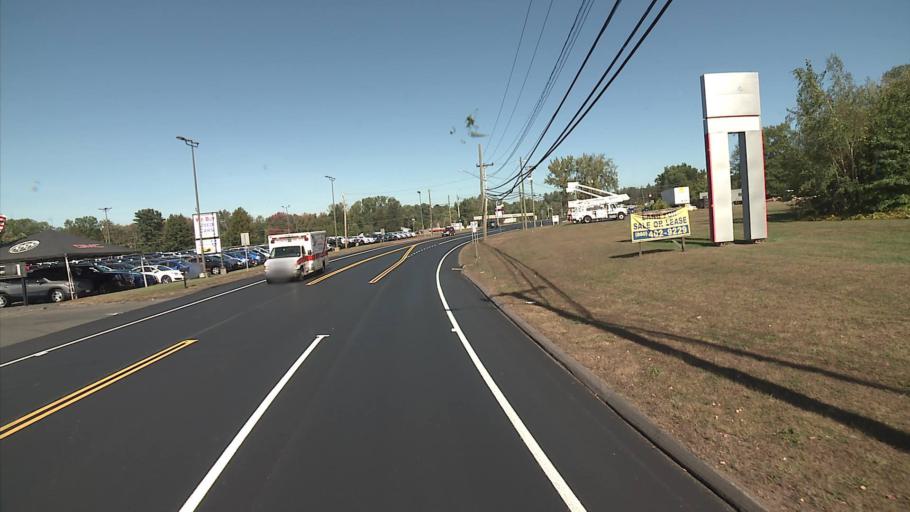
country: US
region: Connecticut
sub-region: Tolland County
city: Rockville
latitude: 41.8627
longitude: -72.4813
